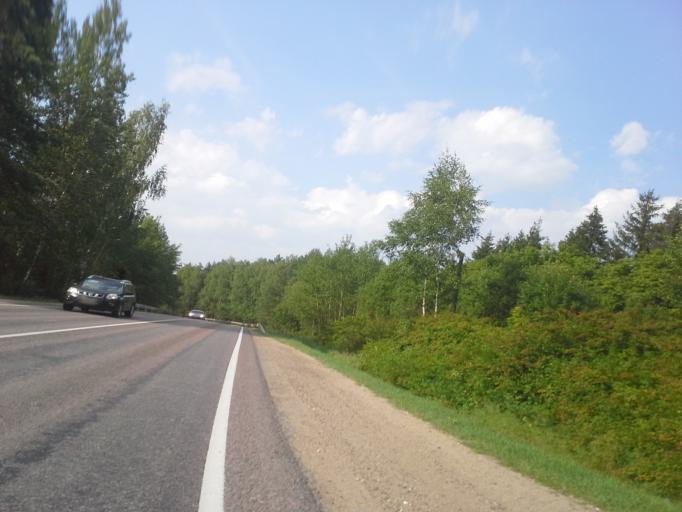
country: RU
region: Moskovskaya
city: Istra
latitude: 55.8824
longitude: 36.7990
